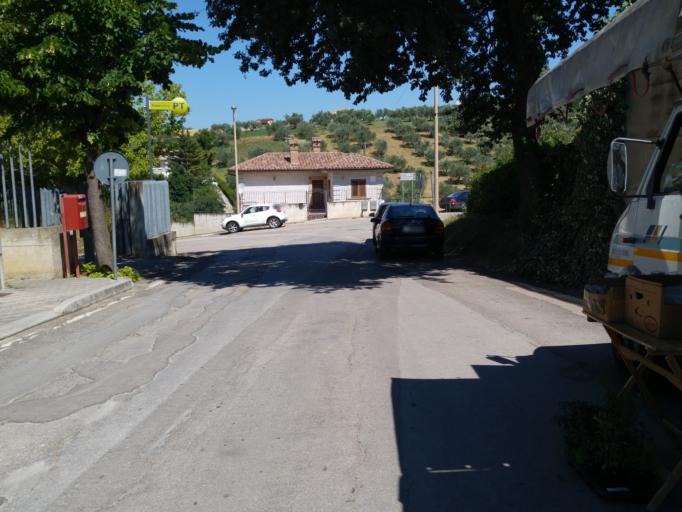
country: IT
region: Abruzzo
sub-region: Provincia di Pescara
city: Elice
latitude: 42.5218
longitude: 13.9698
